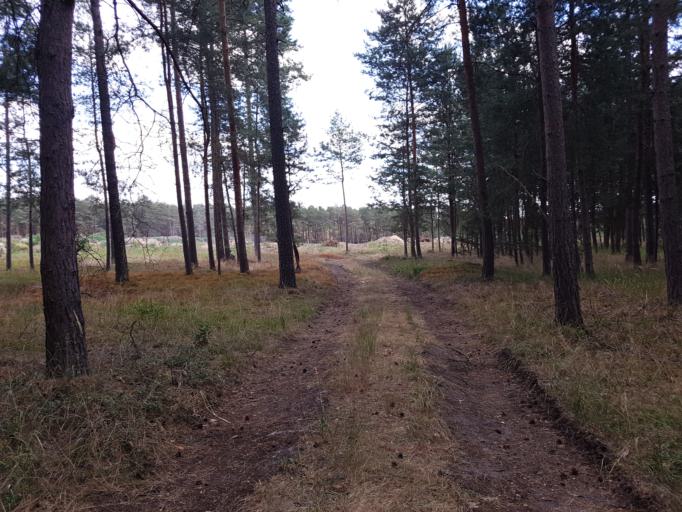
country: DE
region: Brandenburg
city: Cottbus
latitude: 51.7122
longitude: 14.4439
